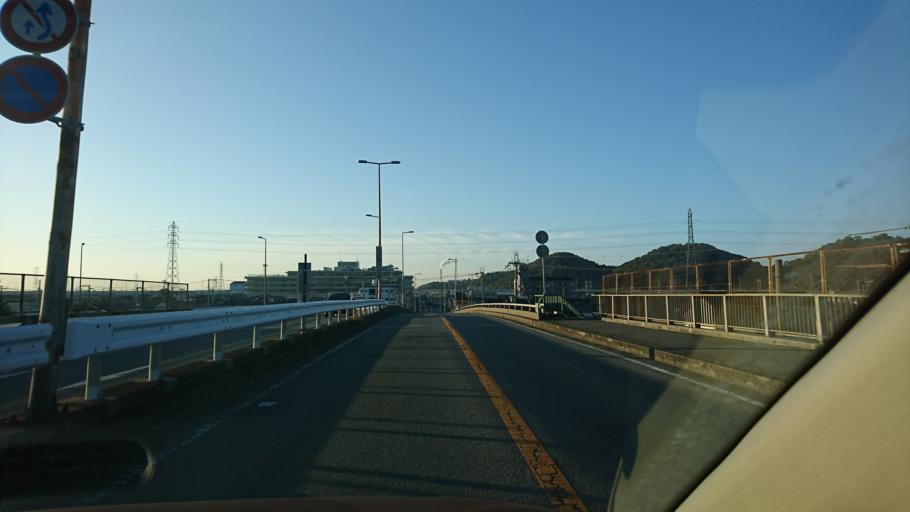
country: JP
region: Hyogo
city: Shirahamacho-usazakiminami
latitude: 34.7929
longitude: 134.7719
